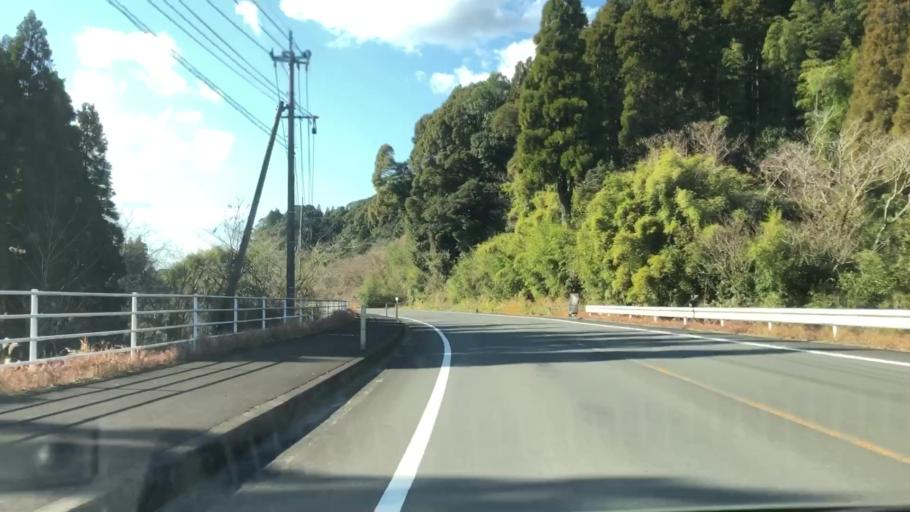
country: JP
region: Kagoshima
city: Satsumasendai
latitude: 31.8625
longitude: 130.4008
